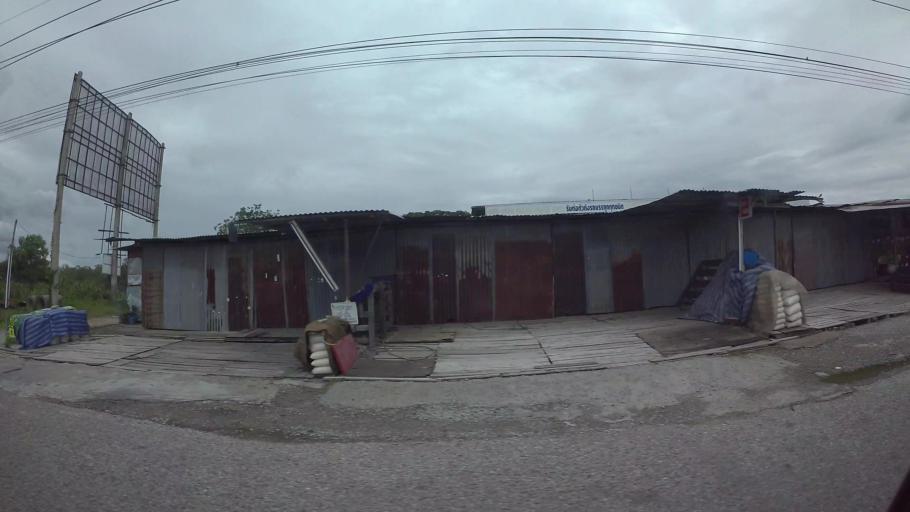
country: TH
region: Chon Buri
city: Si Racha
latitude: 13.1948
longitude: 100.9996
